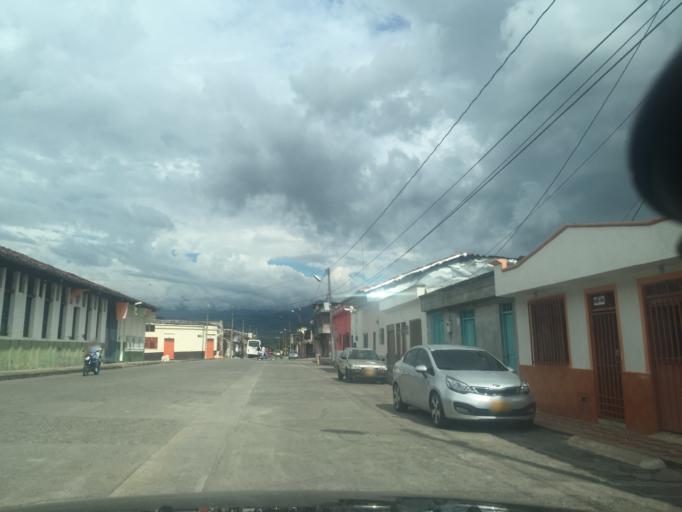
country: CO
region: Valle del Cauca
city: Caicedonia
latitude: 4.3367
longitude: -75.8310
